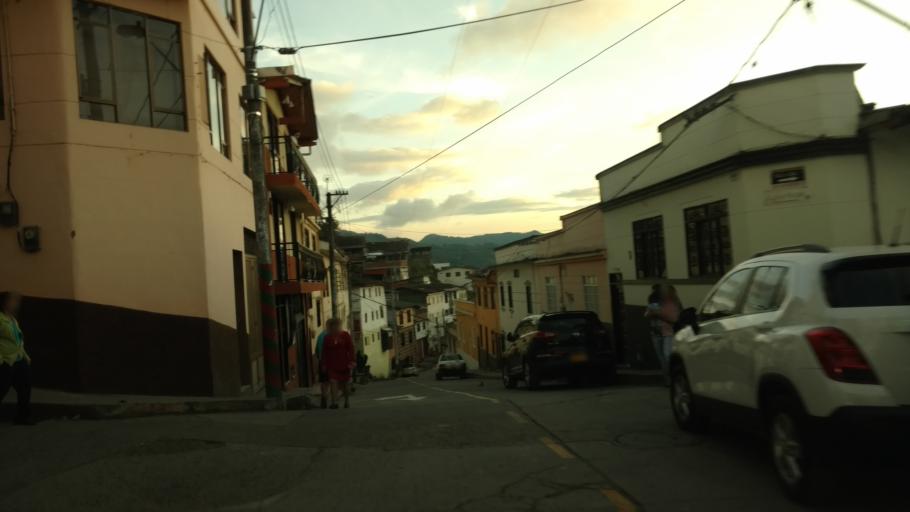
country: CO
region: Caldas
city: Aranzazu
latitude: 5.2717
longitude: -75.4920
